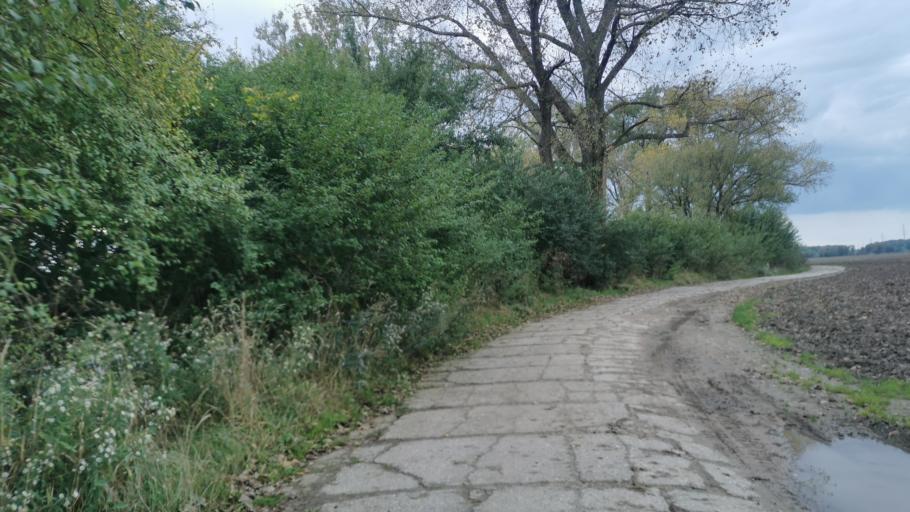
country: SK
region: Trnavsky
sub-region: Okres Skalica
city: Holic
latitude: 48.8395
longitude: 17.1846
